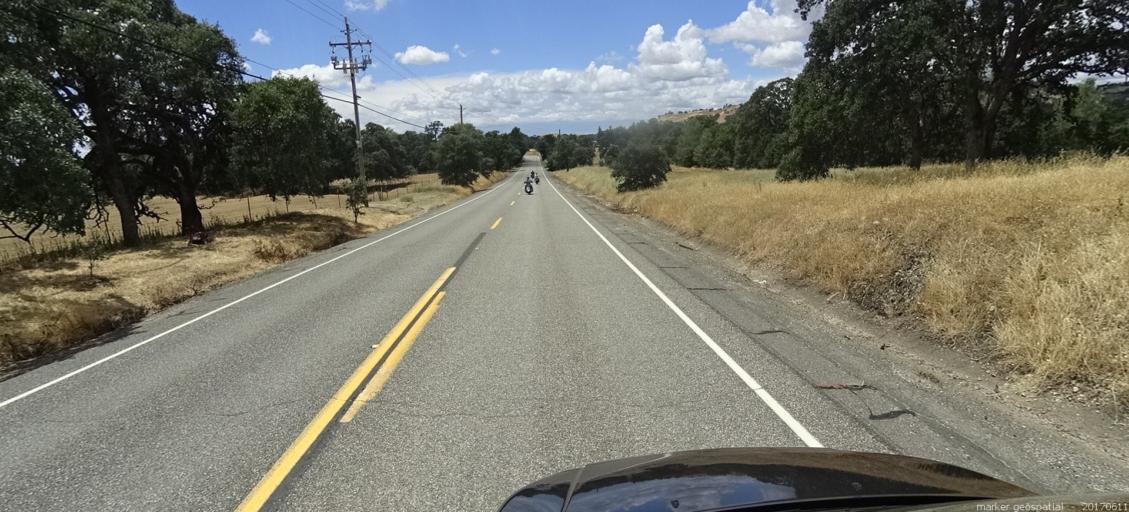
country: US
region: California
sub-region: Butte County
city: Paradise
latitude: 39.6563
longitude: -121.5780
